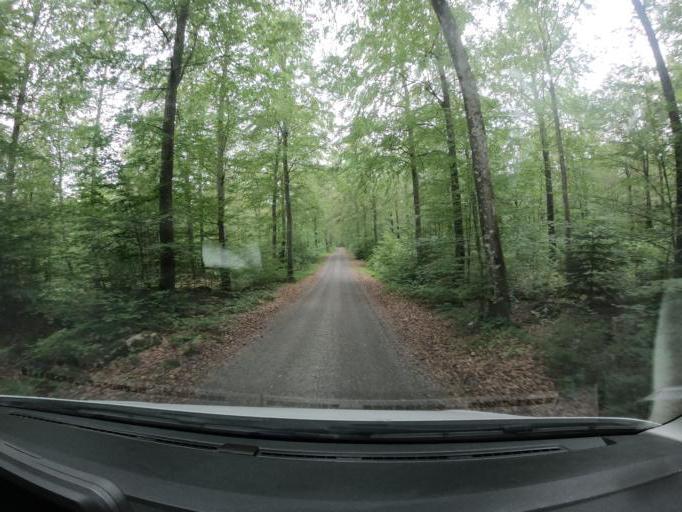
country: SE
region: Skane
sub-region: Perstorps Kommun
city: Perstorp
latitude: 56.1033
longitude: 13.5318
